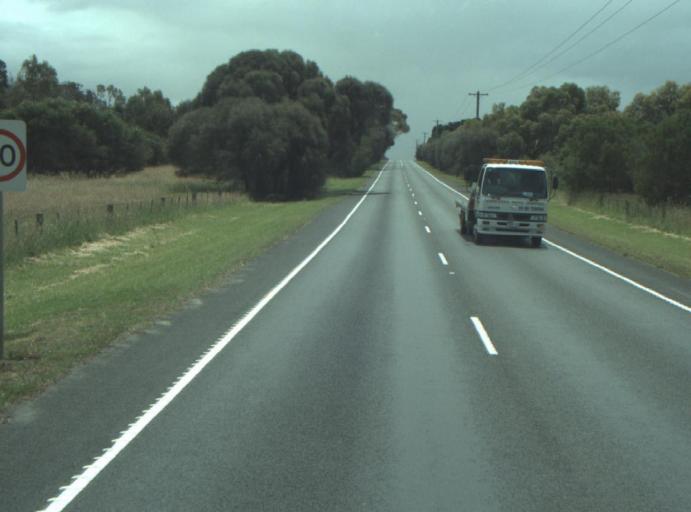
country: AU
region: Victoria
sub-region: Greater Geelong
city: Wandana Heights
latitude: -38.2346
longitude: 144.2793
